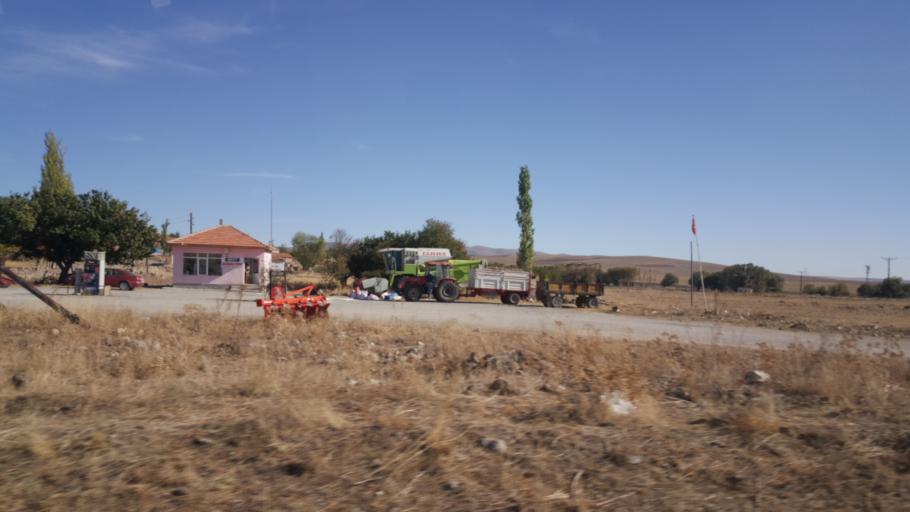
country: TR
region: Ankara
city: Altpinar
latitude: 39.2429
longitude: 32.7435
